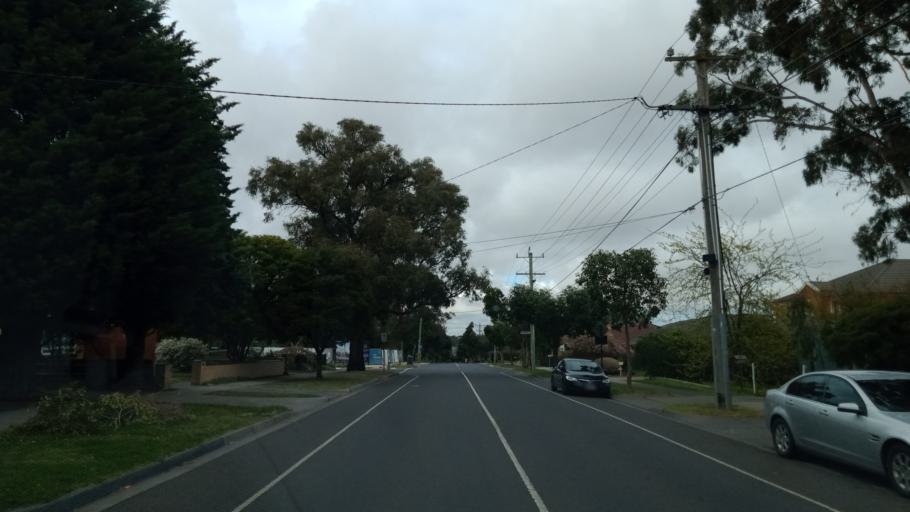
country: AU
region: Victoria
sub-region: Monash
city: Notting Hill
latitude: -37.8782
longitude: 145.1410
